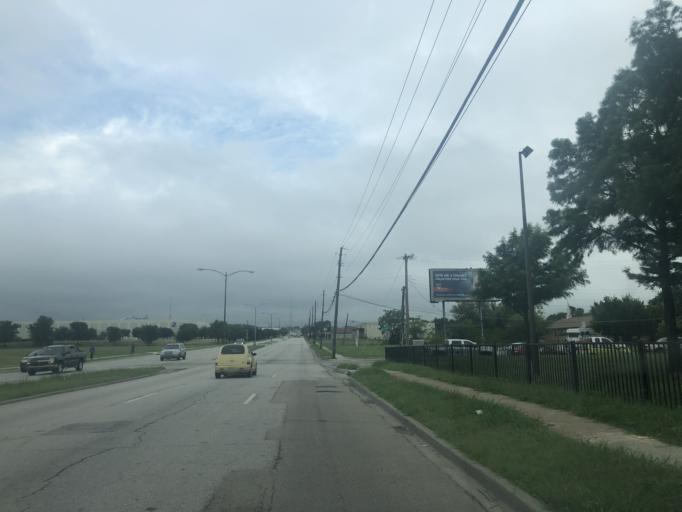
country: US
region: Texas
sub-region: Dallas County
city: Cockrell Hill
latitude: 32.7851
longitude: -96.8739
